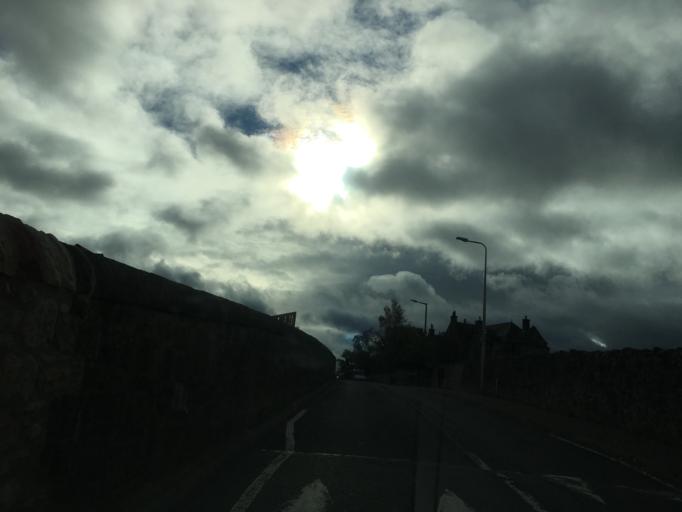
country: GB
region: Scotland
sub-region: Midlothian
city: Loanhead
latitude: 55.9099
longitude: -3.1686
